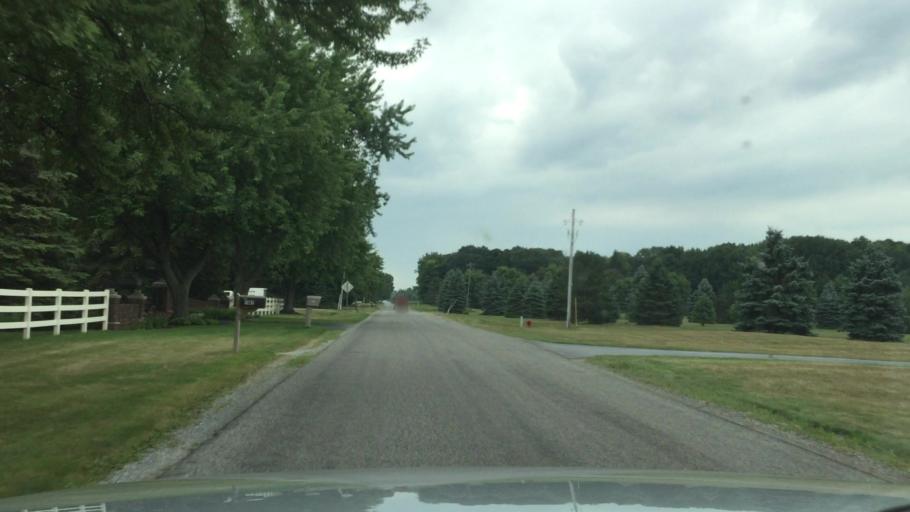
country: US
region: Michigan
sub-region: Saginaw County
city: Frankenmuth
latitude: 43.3206
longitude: -83.7958
